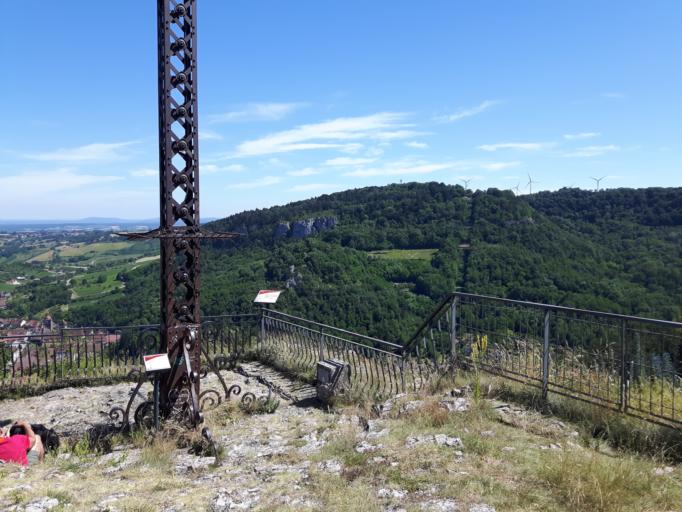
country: FR
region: Franche-Comte
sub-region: Departement du Jura
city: Poligny
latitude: 46.8293
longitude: 5.7082
